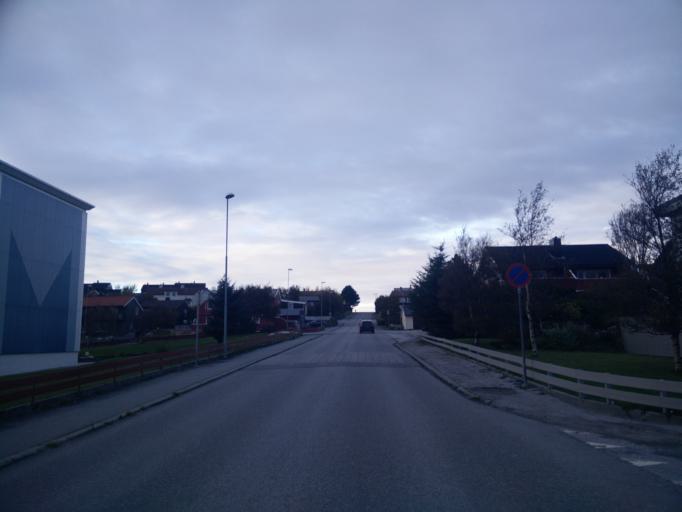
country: NO
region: More og Romsdal
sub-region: Kristiansund
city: Kristiansund
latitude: 63.1230
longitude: 7.7149
